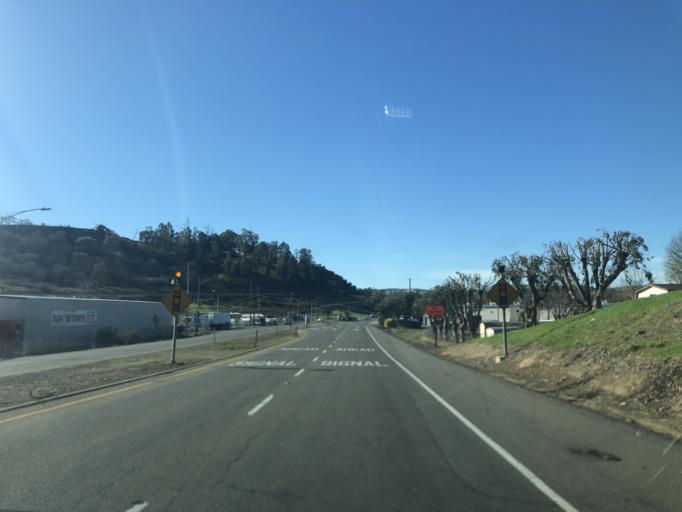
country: US
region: California
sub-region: Contra Costa County
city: Vine Hill
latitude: 38.0076
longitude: -122.0875
